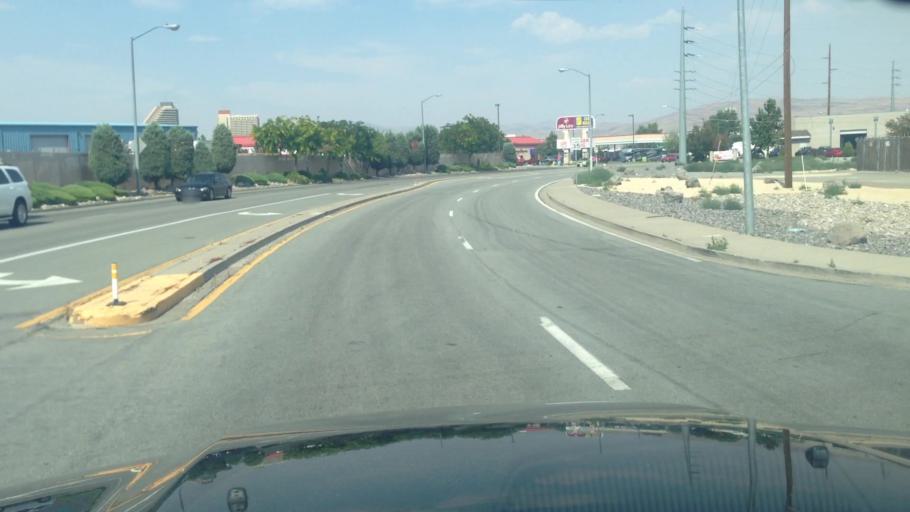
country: US
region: Nevada
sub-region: Washoe County
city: Sparks
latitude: 39.5229
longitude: -119.7702
